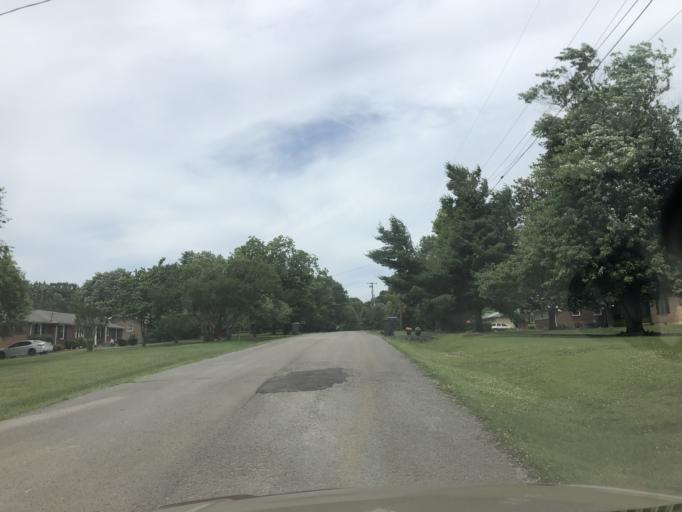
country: US
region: Tennessee
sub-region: Davidson County
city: Lakewood
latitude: 36.2581
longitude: -86.6079
